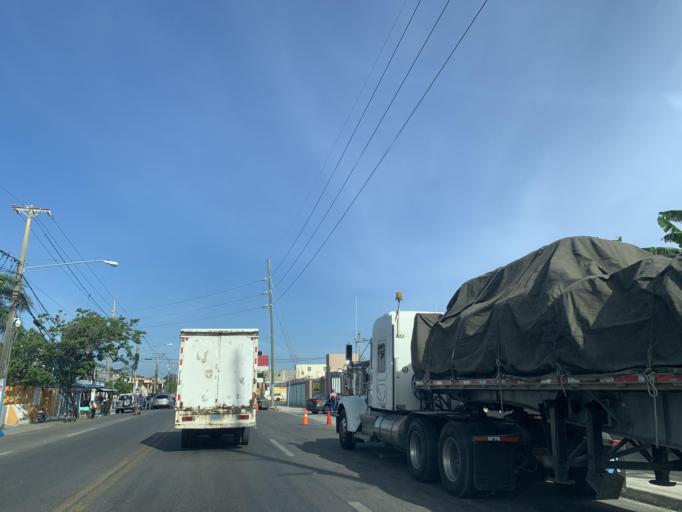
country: DO
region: Puerto Plata
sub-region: Puerto Plata
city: Puerto Plata
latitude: 19.7975
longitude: -70.7010
